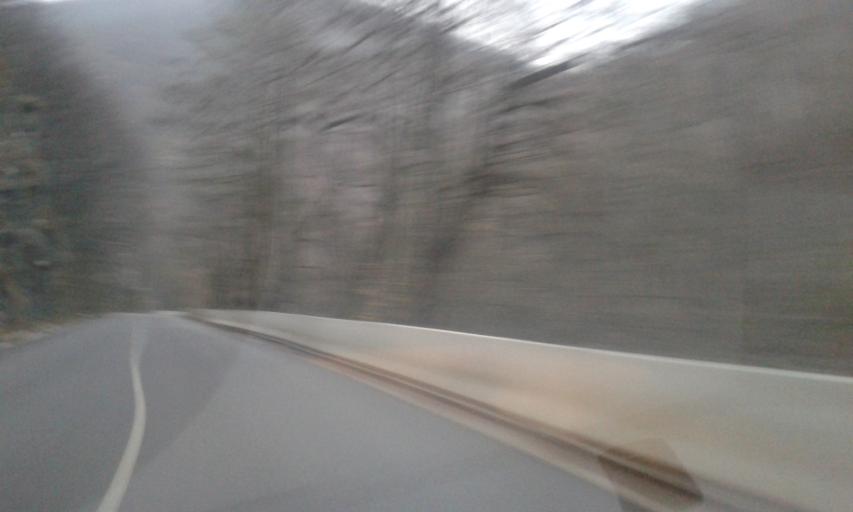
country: RO
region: Gorj
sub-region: Comuna Bumbesti-Jiu
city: Bumbesti-Jiu
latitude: 45.2499
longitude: 23.3862
